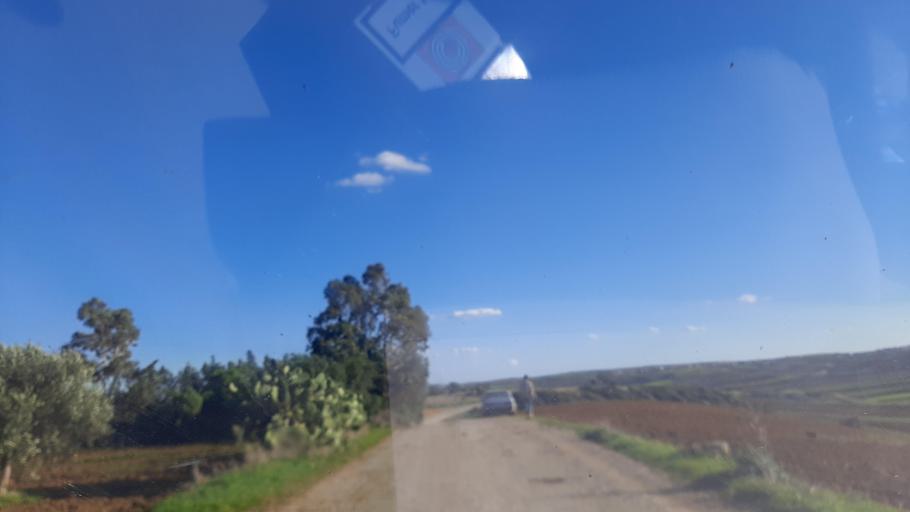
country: TN
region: Nabul
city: El Mida
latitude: 36.8366
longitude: 10.8332
